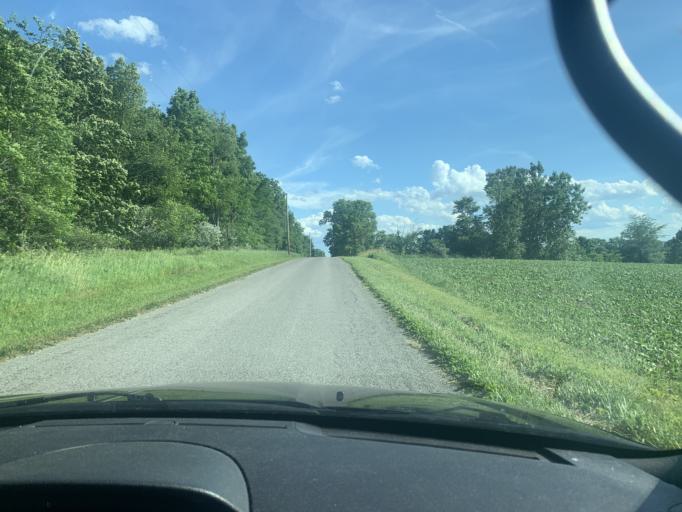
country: US
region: Ohio
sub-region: Logan County
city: De Graff
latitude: 40.3084
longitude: -83.8746
